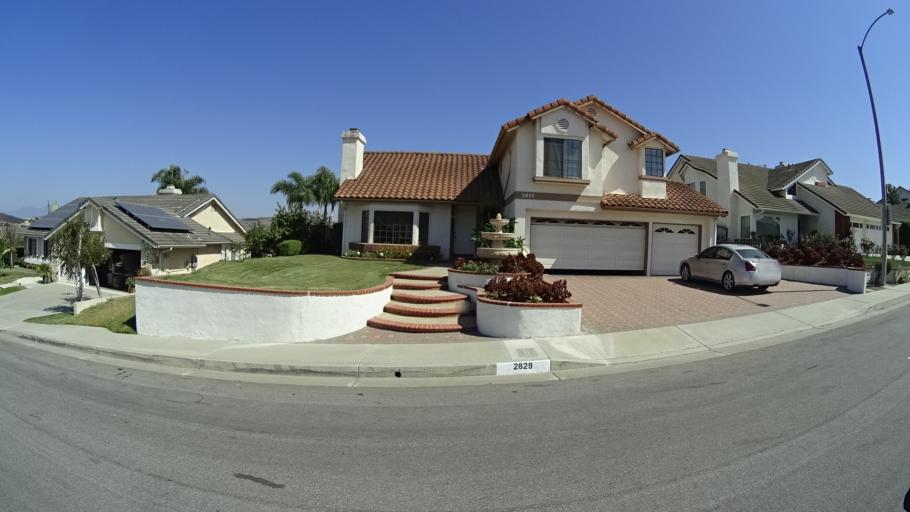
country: US
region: California
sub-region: Orange County
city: San Clemente
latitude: 33.4637
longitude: -117.6344
